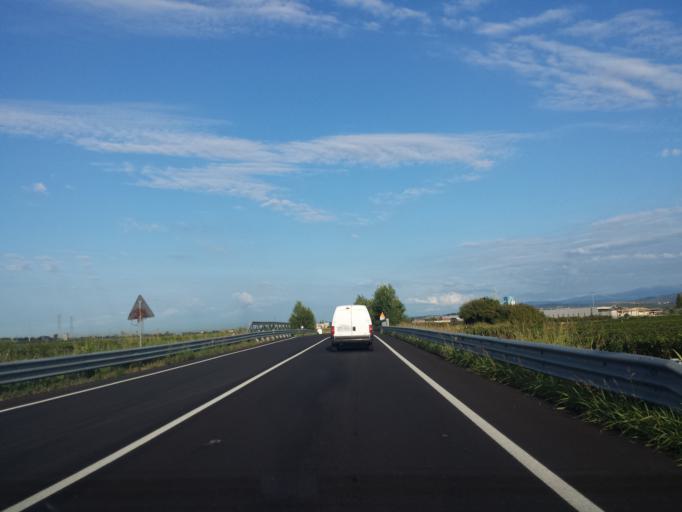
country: IT
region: Veneto
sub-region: Provincia di Verona
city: Belfiore
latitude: 45.3905
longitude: 11.2316
